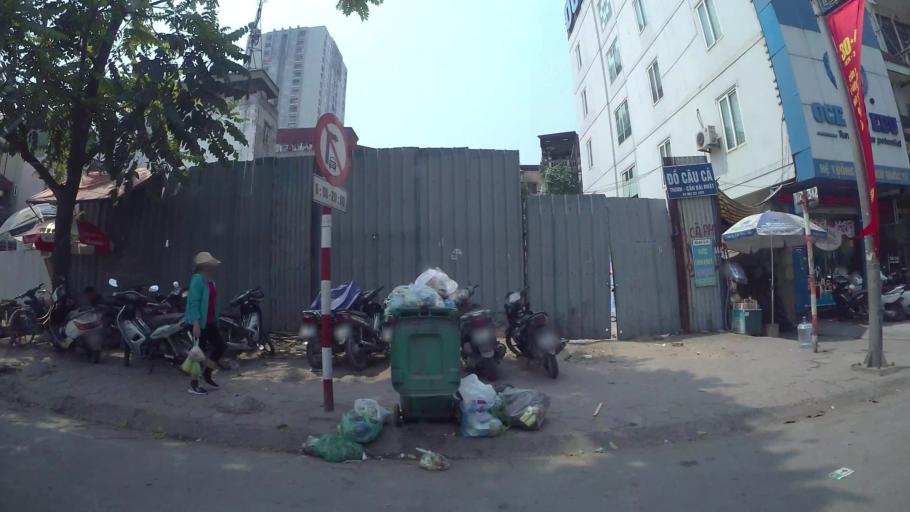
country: VN
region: Ha Noi
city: Thanh Xuan
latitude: 20.9969
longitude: 105.8106
